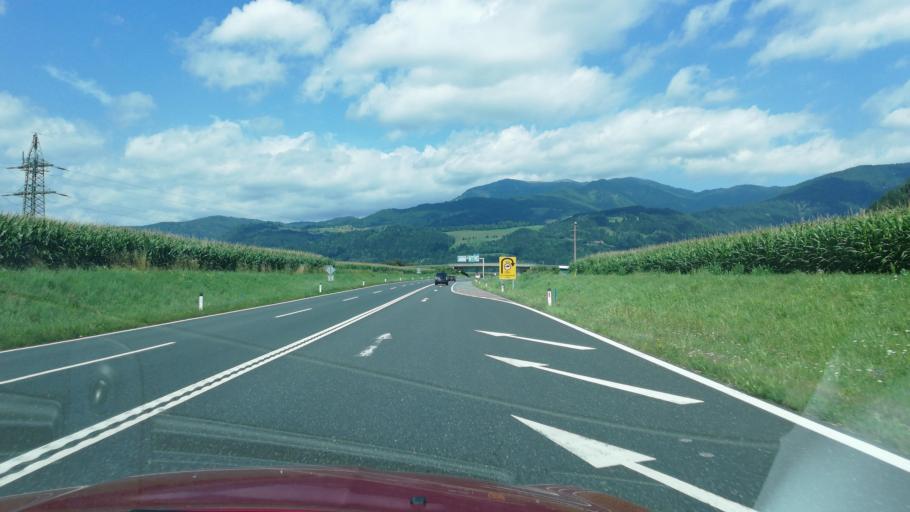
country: AT
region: Carinthia
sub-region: Politischer Bezirk Sankt Veit an der Glan
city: Friesach
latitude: 46.9634
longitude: 14.4032
